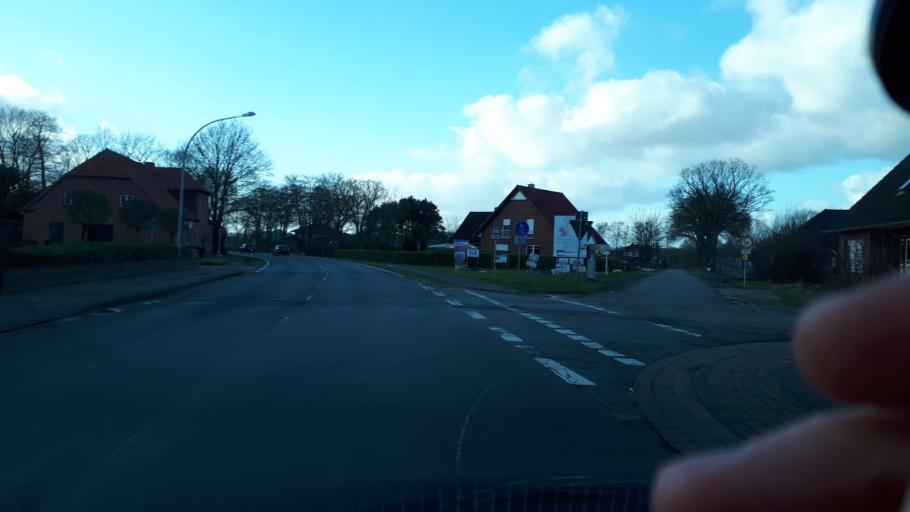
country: DE
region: Lower Saxony
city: Molbergen
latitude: 52.8641
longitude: 7.9118
